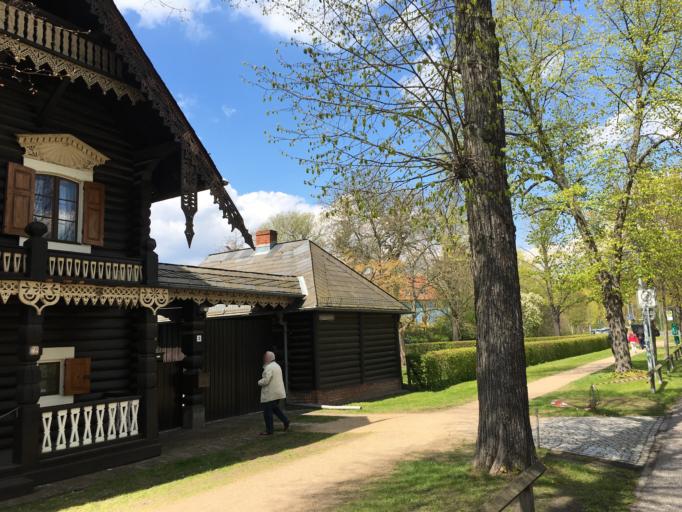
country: DE
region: Brandenburg
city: Potsdam
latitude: 52.4116
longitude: 13.0566
